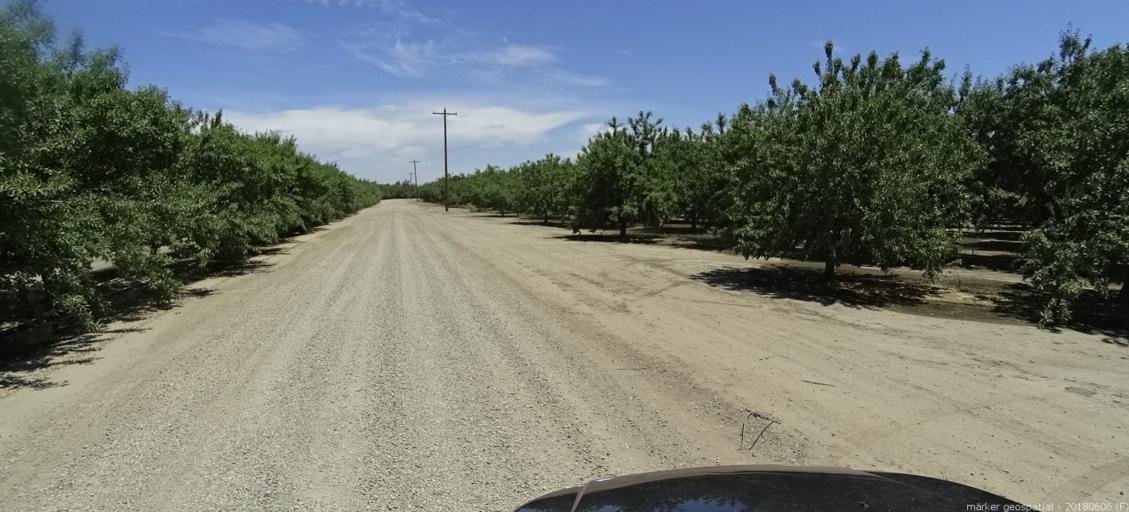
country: US
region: California
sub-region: Fresno County
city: Mendota
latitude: 36.7999
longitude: -120.3561
